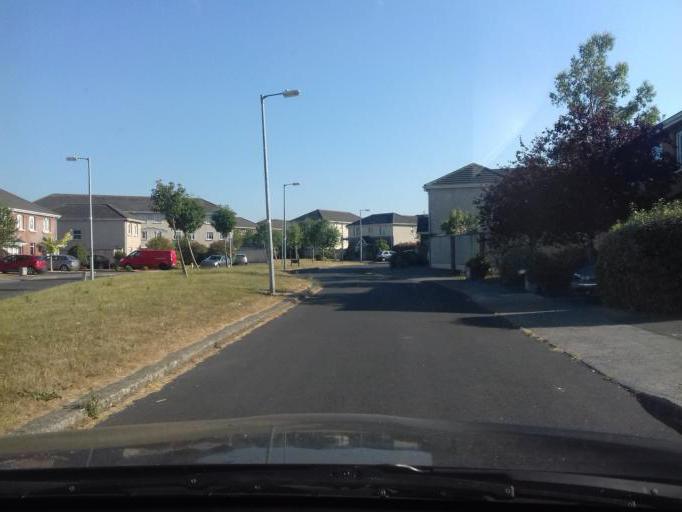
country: IE
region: Leinster
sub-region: Fingal County
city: Blanchardstown
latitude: 53.4232
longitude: -6.3910
